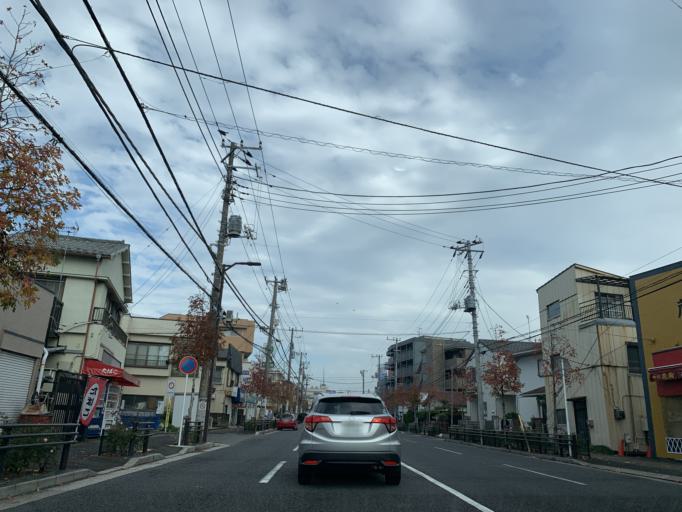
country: JP
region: Chiba
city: Funabashi
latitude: 35.7161
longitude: 139.9314
